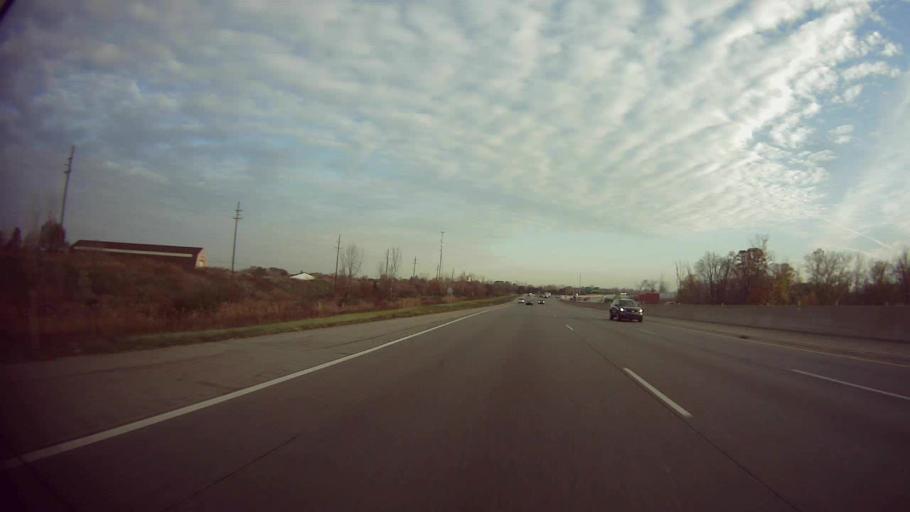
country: US
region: Michigan
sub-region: Macomb County
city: Mount Clemens
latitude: 42.5496
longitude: -82.8780
